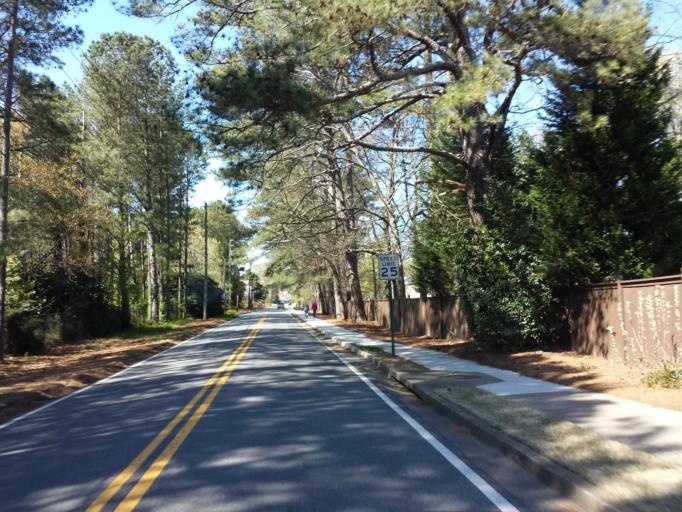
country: US
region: Georgia
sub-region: Cobb County
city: Smyrna
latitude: 33.9357
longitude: -84.4806
